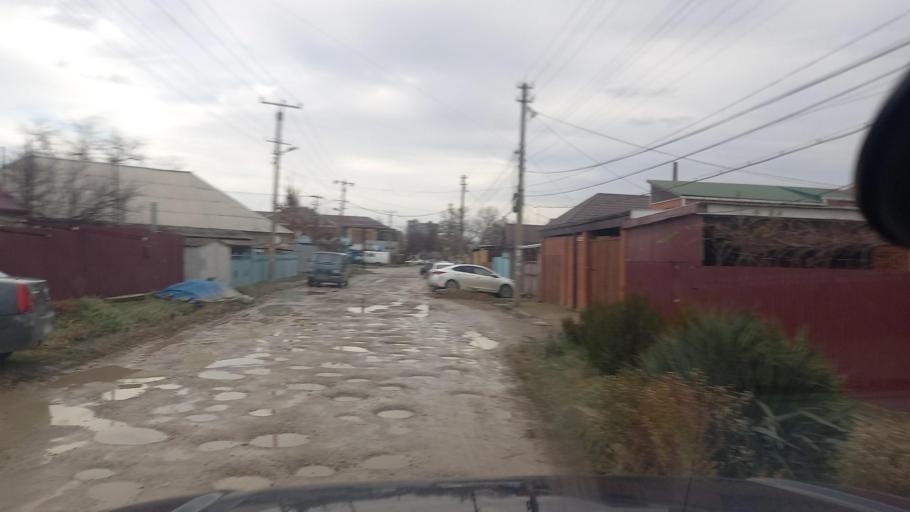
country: RU
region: Adygeya
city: Yablonovskiy
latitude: 44.9883
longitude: 38.9495
